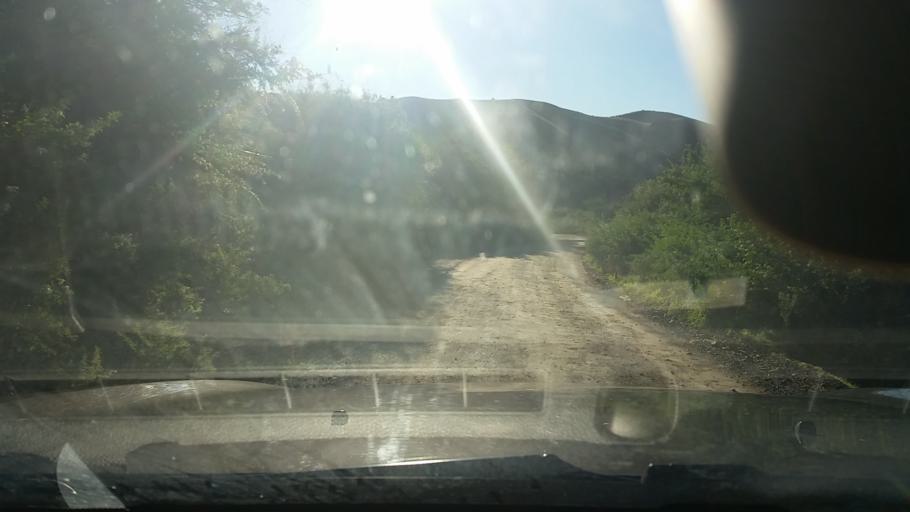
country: NZ
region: Marlborough
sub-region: Marlborough District
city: Blenheim
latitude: -41.5825
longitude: 174.0650
